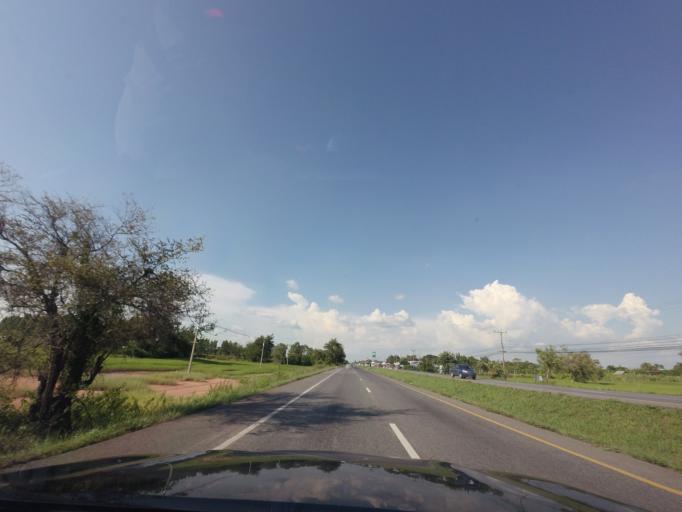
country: TH
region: Khon Kaen
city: Non Sila
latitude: 15.9899
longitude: 102.6985
